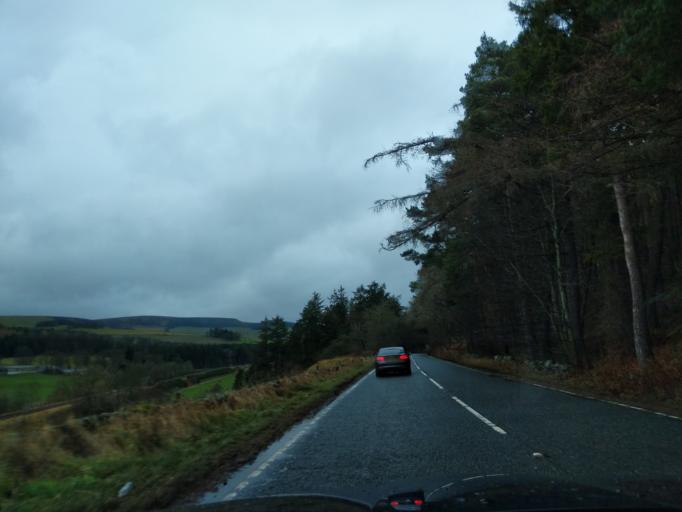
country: GB
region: Scotland
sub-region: The Scottish Borders
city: Galashiels
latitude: 55.6481
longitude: -2.8587
